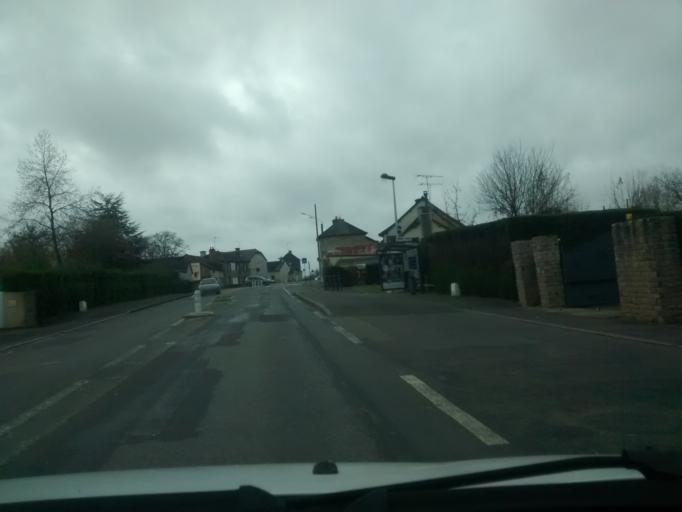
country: FR
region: Brittany
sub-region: Departement d'Ille-et-Vilaine
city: Fouillard
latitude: 48.1606
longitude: -1.5856
